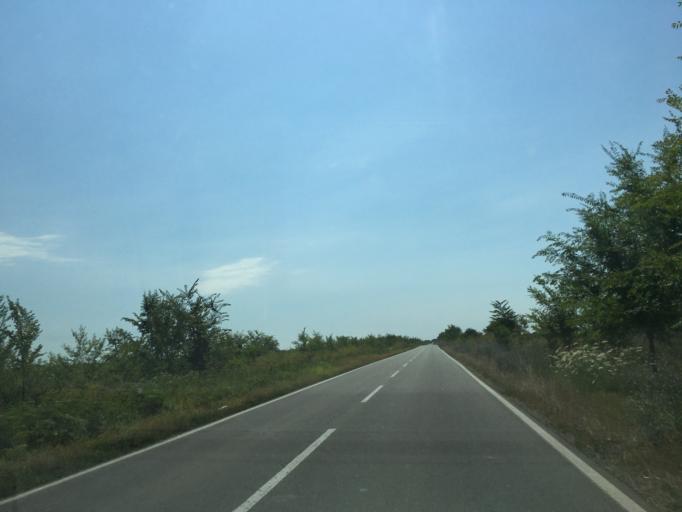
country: RS
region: Central Serbia
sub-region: Belgrade
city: Grocka
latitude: 44.7475
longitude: 20.7574
